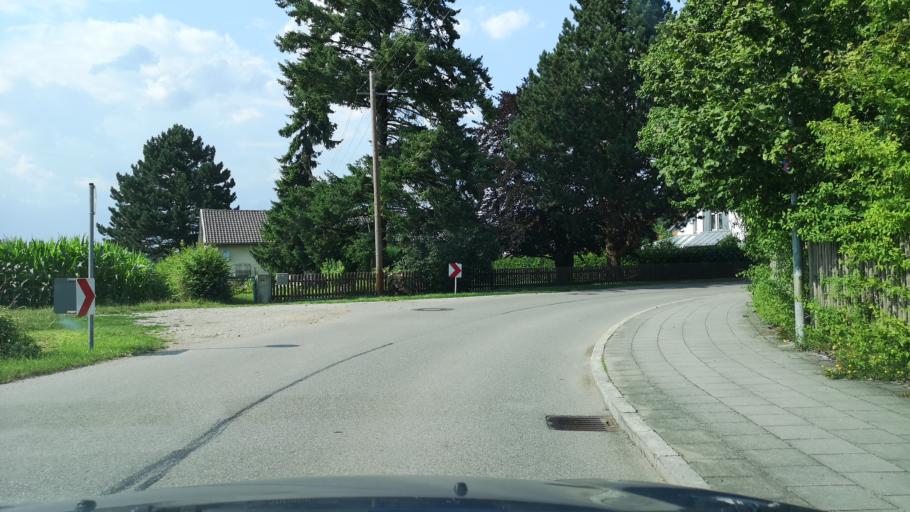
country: DE
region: Bavaria
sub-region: Upper Bavaria
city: Kirchheim bei Muenchen
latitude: 48.1754
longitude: 11.7408
